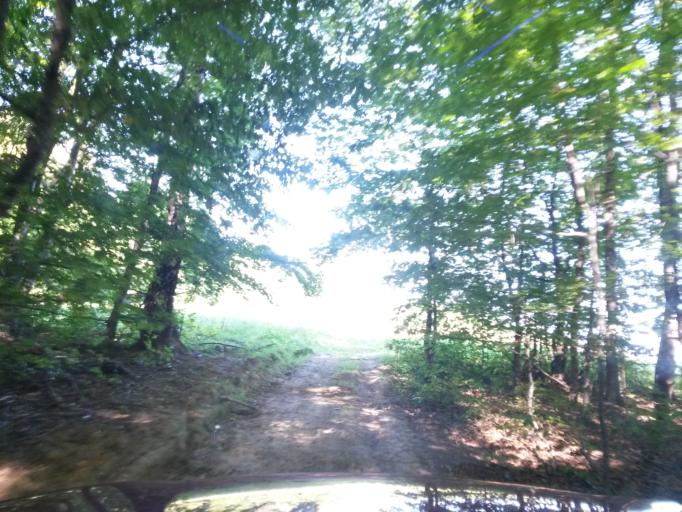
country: SK
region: Presovsky
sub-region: Okres Presov
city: Presov
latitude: 48.9834
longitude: 21.1472
